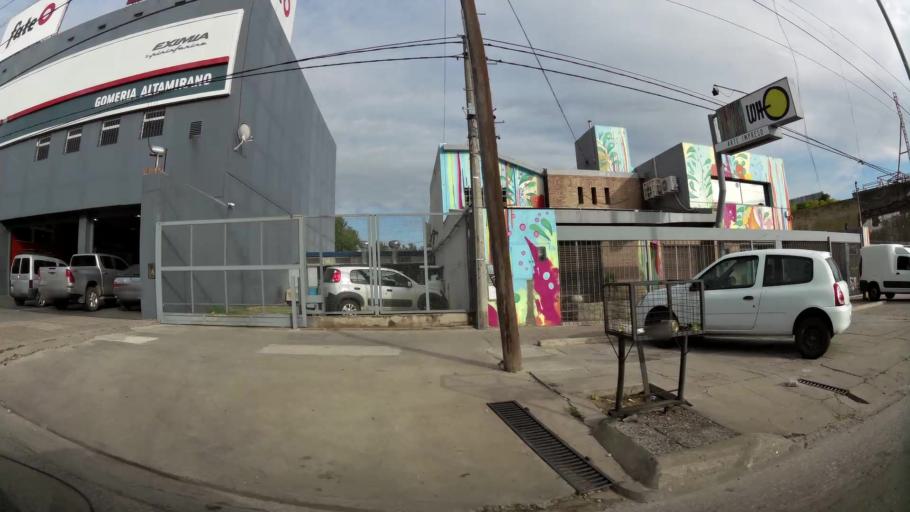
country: AR
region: Cordoba
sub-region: Departamento de Capital
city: Cordoba
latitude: -31.4342
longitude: -64.1948
